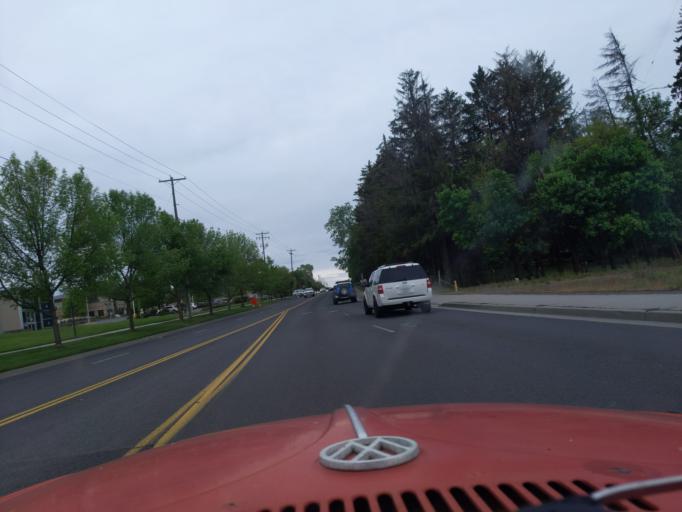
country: US
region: Washington
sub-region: Spokane County
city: Spokane
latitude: 47.6151
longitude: -117.3685
